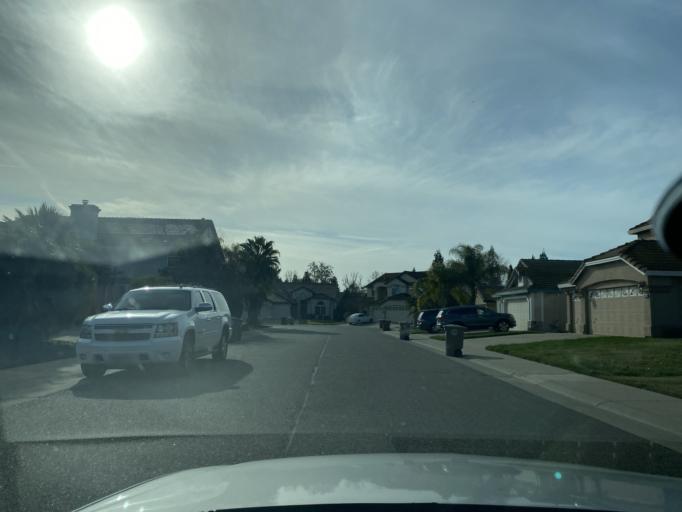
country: US
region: California
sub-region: Sacramento County
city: Elk Grove
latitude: 38.4398
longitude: -121.3805
